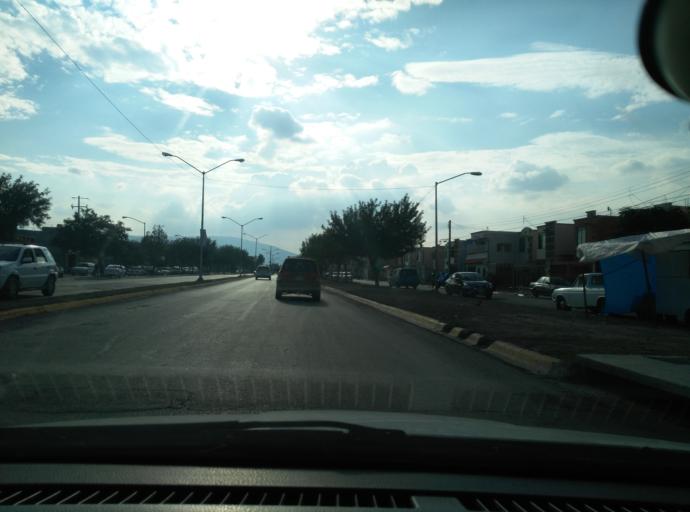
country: MX
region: Nuevo Leon
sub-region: Apodaca
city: Fraccionamiento Cosmopolis Octavo Sector
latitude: 25.7675
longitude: -100.2421
